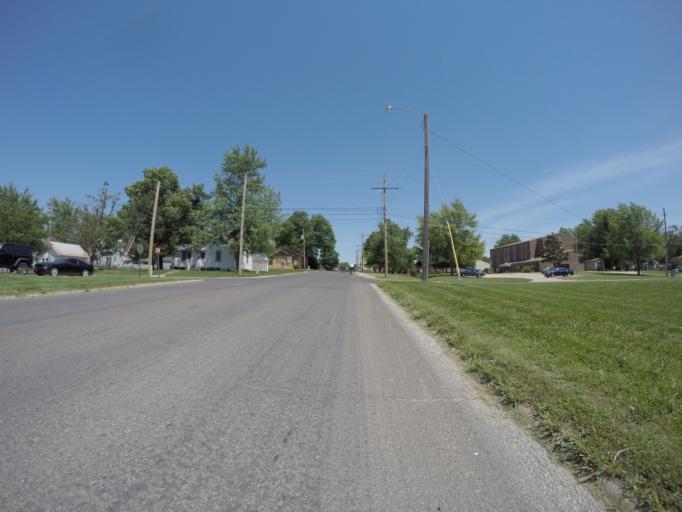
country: US
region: Kansas
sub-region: Nemaha County
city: Sabetha
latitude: 39.8998
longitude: -95.8039
